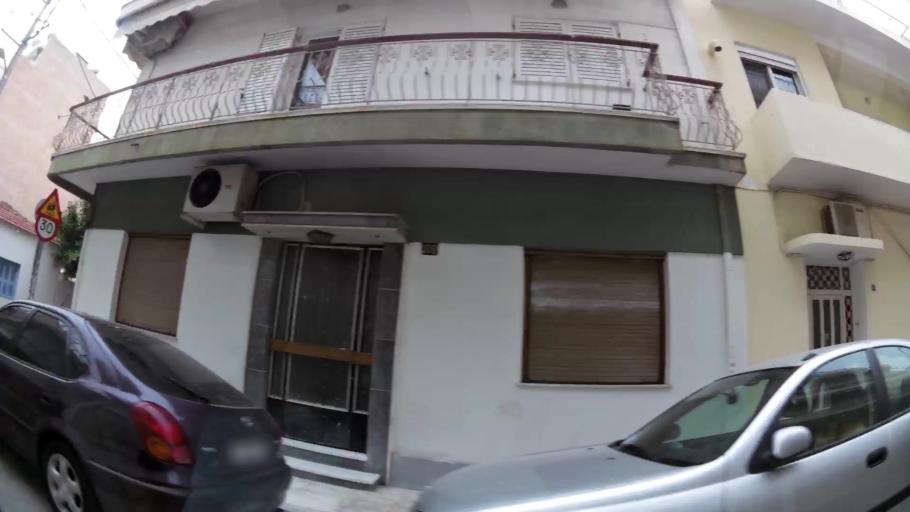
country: GR
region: Attica
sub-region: Nomos Piraios
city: Agios Ioannis Rentis
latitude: 37.9656
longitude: 23.6591
